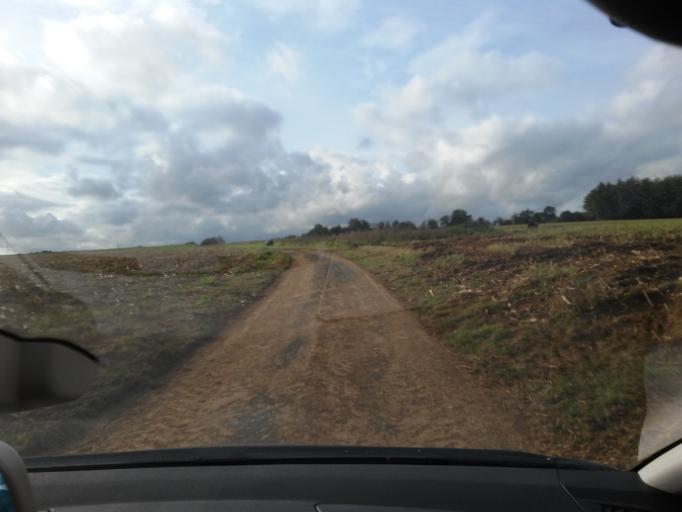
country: BE
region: Wallonia
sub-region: Province du Luxembourg
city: Arlon
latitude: 49.7143
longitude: 5.8078
